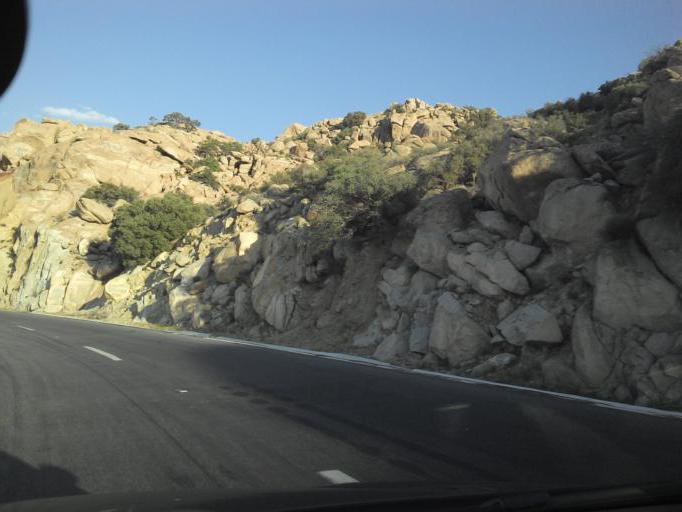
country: MX
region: Baja California
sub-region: Tecate
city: Cereso del Hongo
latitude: 32.5777
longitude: -116.0377
